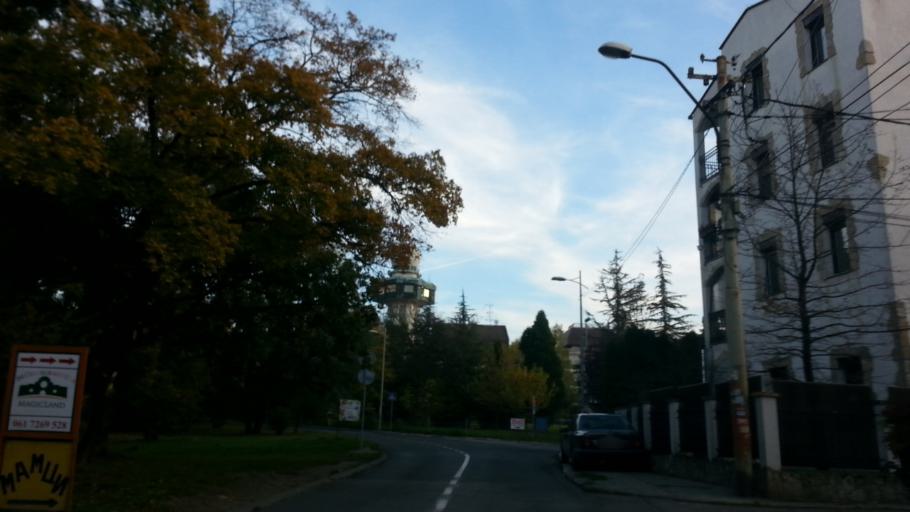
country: RS
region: Central Serbia
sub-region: Belgrade
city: Cukarica
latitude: 44.7732
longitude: 20.4238
